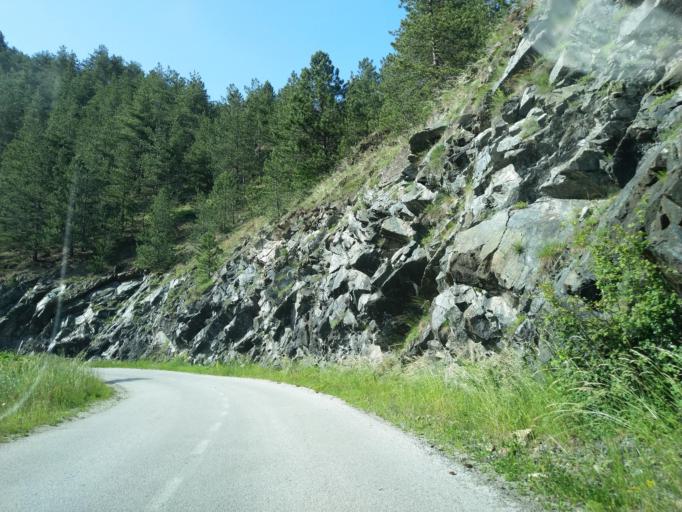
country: RS
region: Central Serbia
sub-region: Zlatiborski Okrug
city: Bajina Basta
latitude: 43.8495
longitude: 19.6218
